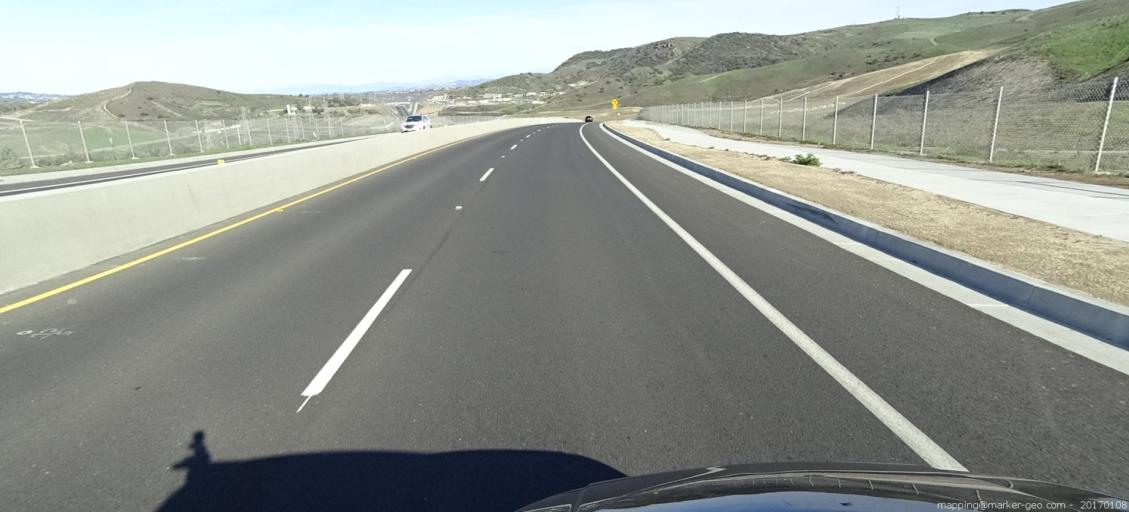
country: US
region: California
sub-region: Orange County
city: San Clemente
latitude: 33.4802
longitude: -117.6089
